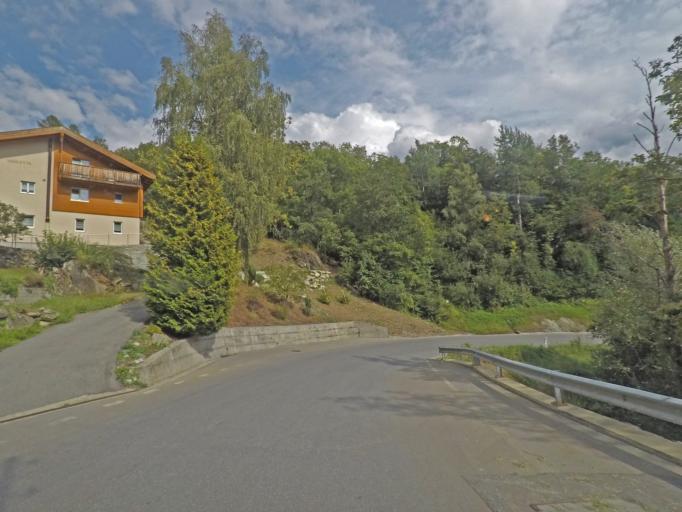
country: CH
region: Valais
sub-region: Brig District
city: Naters
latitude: 46.3376
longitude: 7.9847
